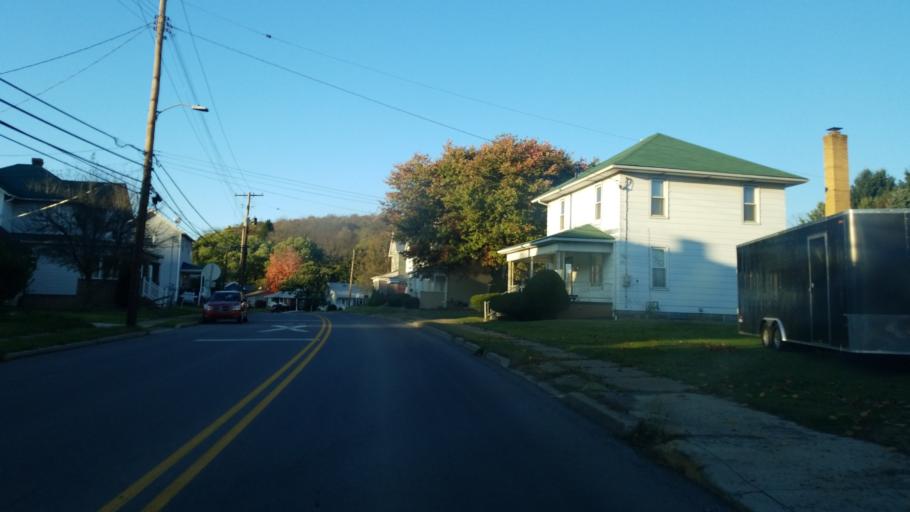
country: US
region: Pennsylvania
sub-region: Jefferson County
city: Punxsutawney
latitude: 40.9527
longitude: -78.9642
